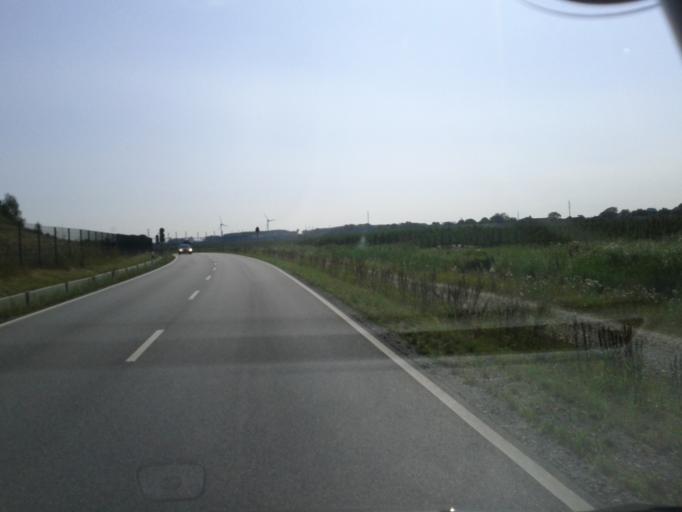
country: DE
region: Lower Saxony
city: Neu Wulmstorf
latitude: 53.5108
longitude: 9.8520
